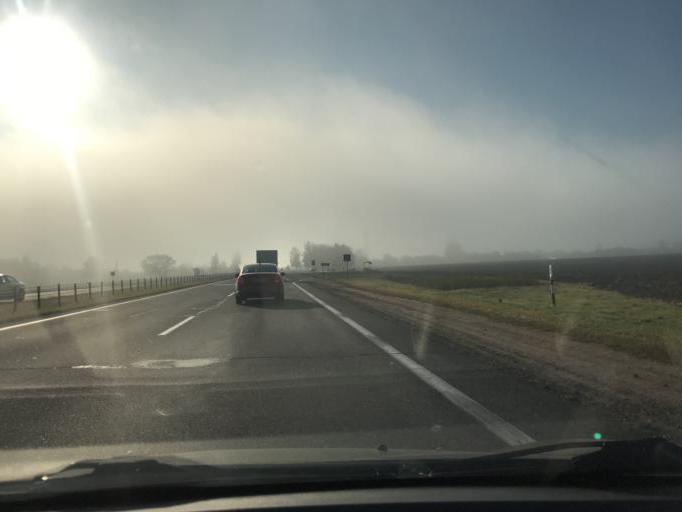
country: BY
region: Minsk
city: Dukora
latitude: 53.6725
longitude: 27.9334
